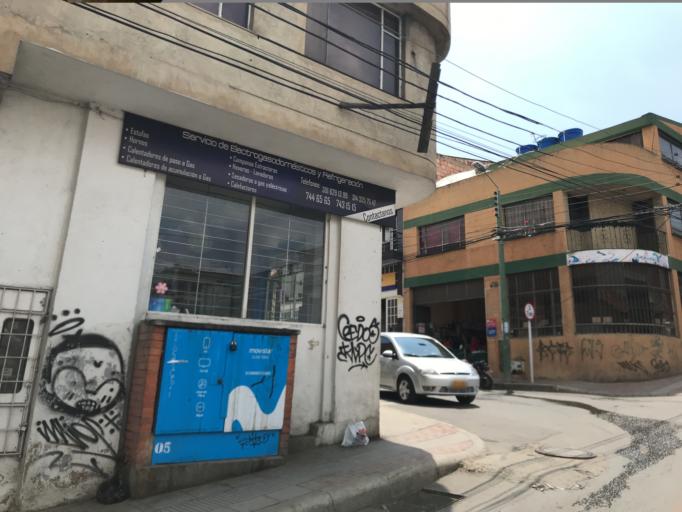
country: CO
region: Boyaca
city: Tunja
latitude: 5.5363
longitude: -73.3649
